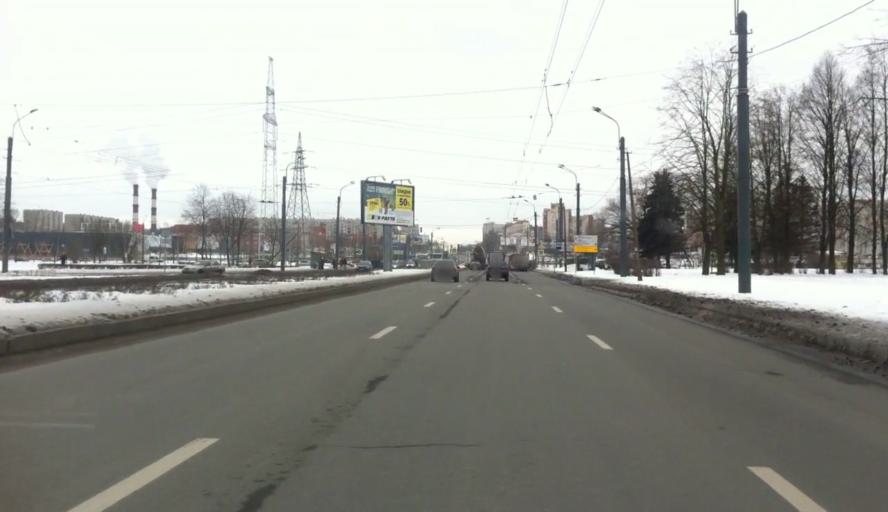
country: RU
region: St.-Petersburg
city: Uritsk
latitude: 59.8490
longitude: 30.1754
